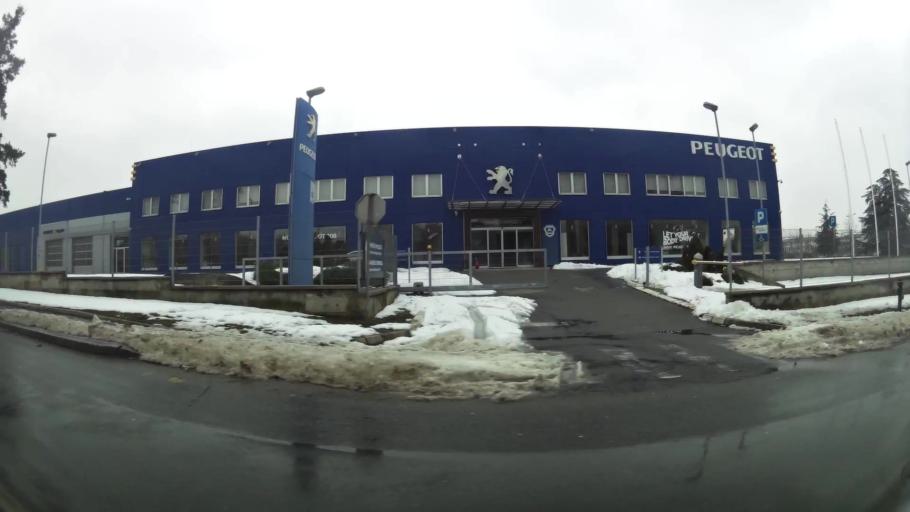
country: RS
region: Central Serbia
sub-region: Belgrade
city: Vozdovac
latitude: 44.7605
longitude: 20.4849
